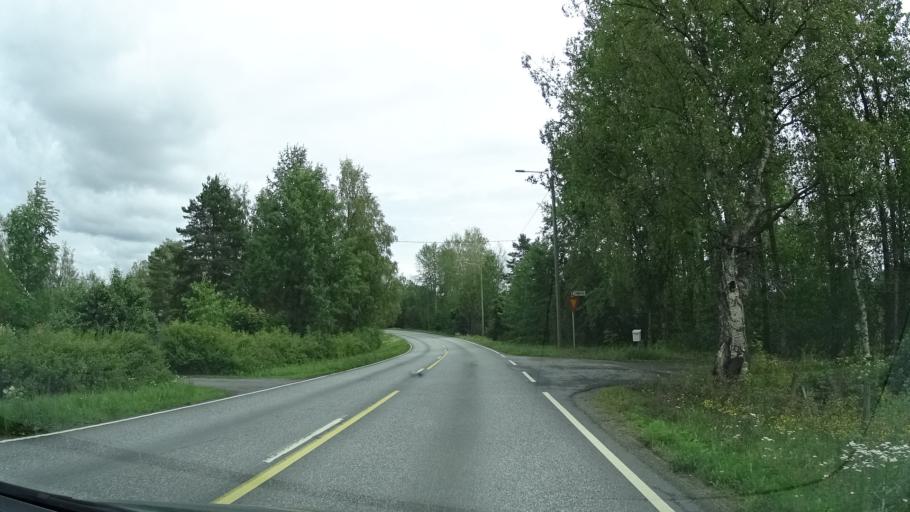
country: FI
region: Pirkanmaa
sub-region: Etelae-Pirkanmaa
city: Urjala
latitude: 61.0825
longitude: 23.4301
